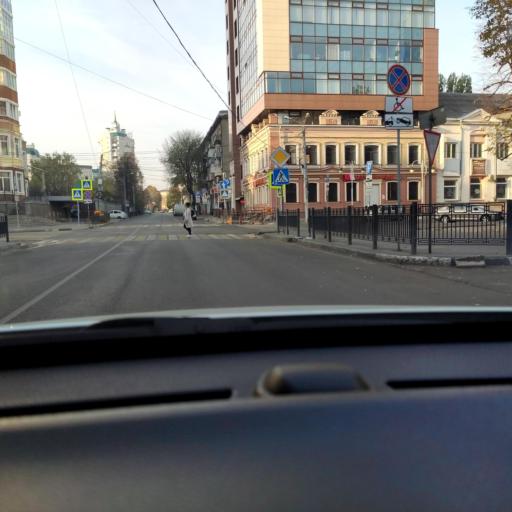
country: RU
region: Voronezj
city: Voronezh
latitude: 51.6646
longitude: 39.1936
